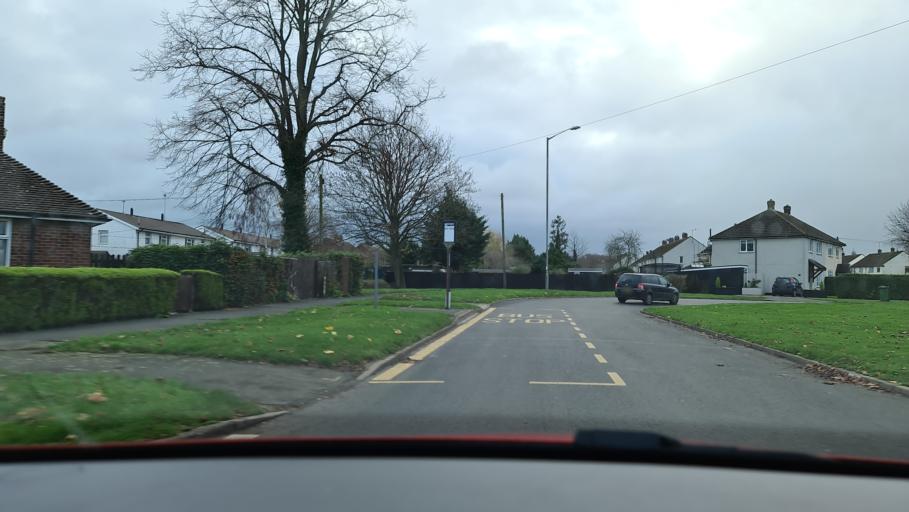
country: GB
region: England
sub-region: Buckinghamshire
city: Aylesbury
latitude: 51.8038
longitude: -0.8163
